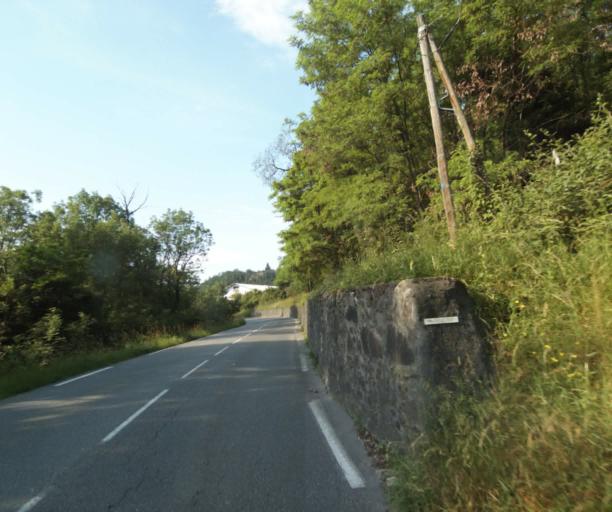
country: FR
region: Rhone-Alpes
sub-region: Departement de la Haute-Savoie
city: Thonon-les-Bains
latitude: 46.3663
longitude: 6.4969
